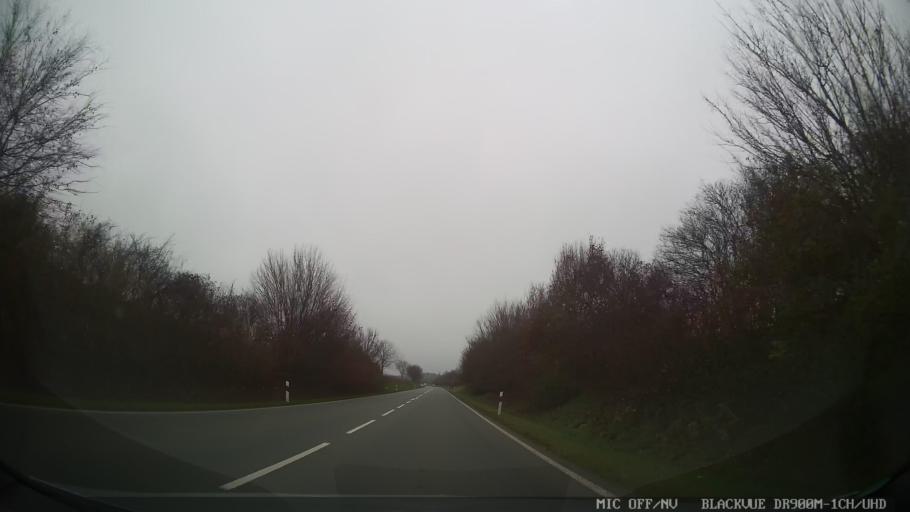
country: DE
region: Bavaria
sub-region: Upper Bavaria
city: Worth
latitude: 48.2479
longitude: 11.8683
